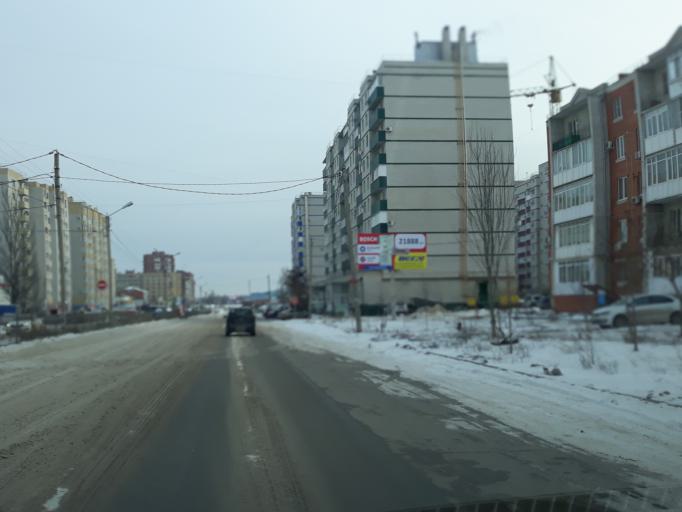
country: RU
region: Rostov
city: Taganrog
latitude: 47.2242
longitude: 38.8585
